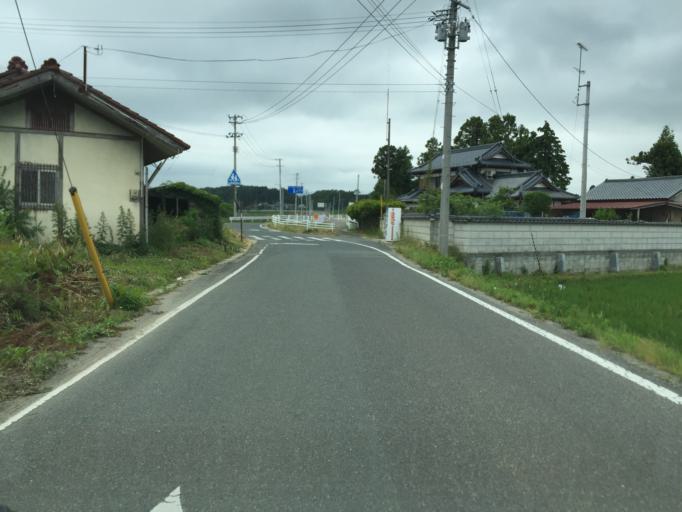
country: JP
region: Miyagi
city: Marumori
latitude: 37.7326
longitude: 140.9287
